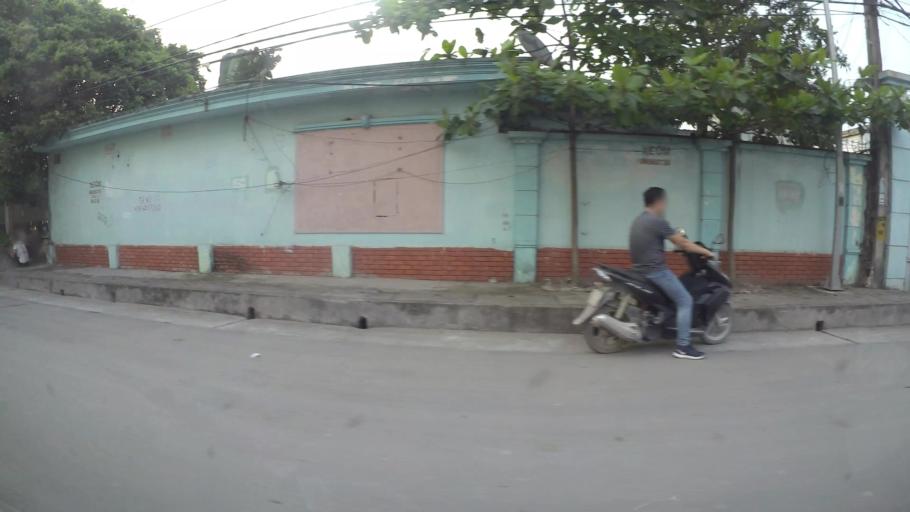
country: VN
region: Ha Noi
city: Cau Dien
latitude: 20.9974
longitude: 105.7267
